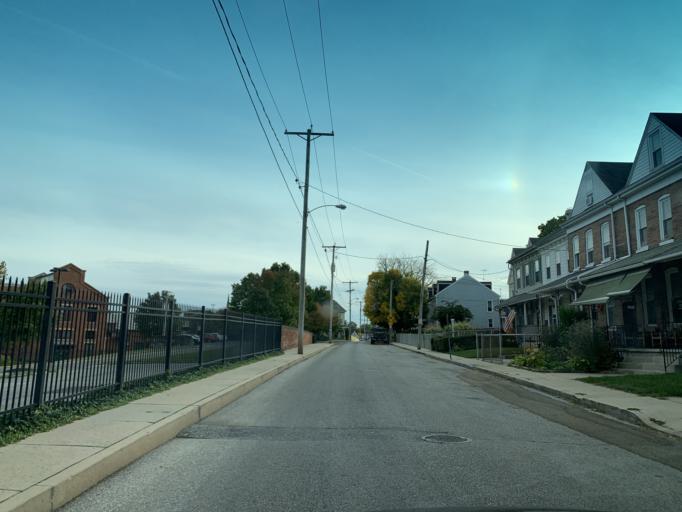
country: US
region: Pennsylvania
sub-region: York County
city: York
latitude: 39.9649
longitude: -76.7349
